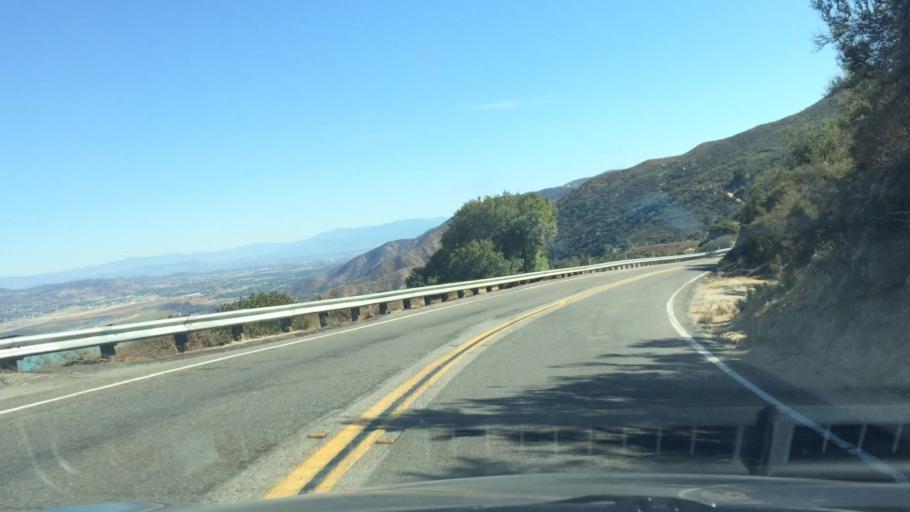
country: US
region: California
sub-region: Riverside County
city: Lakeland Village
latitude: 33.6573
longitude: -117.3976
